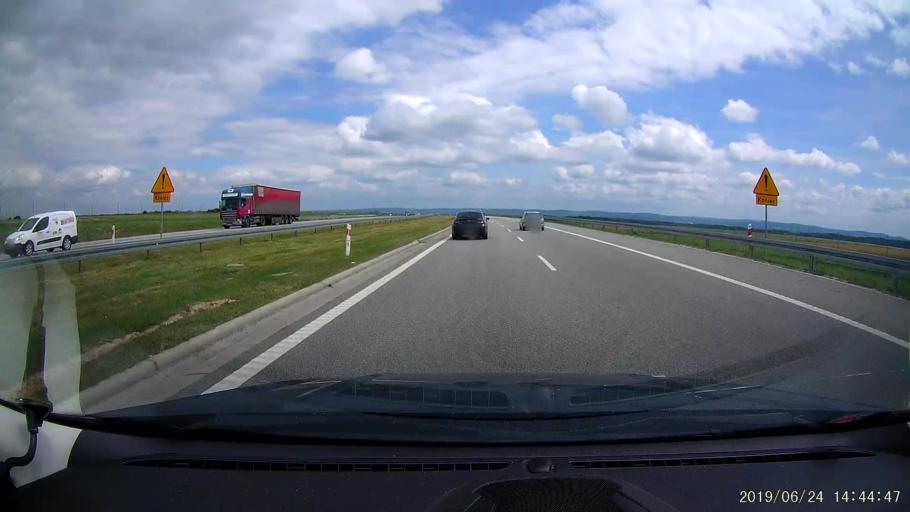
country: PL
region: Subcarpathian Voivodeship
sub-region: Powiat debicki
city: Czarna
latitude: 50.0895
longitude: 21.3041
